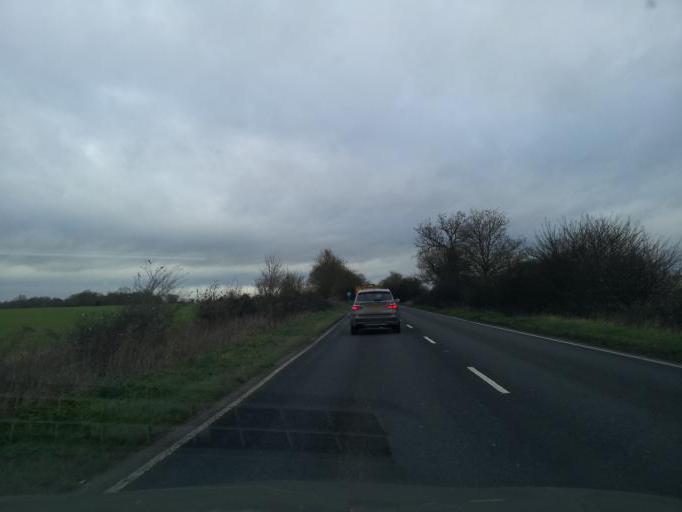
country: GB
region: England
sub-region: Norfolk
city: Long Stratton
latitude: 52.4166
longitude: 1.1991
